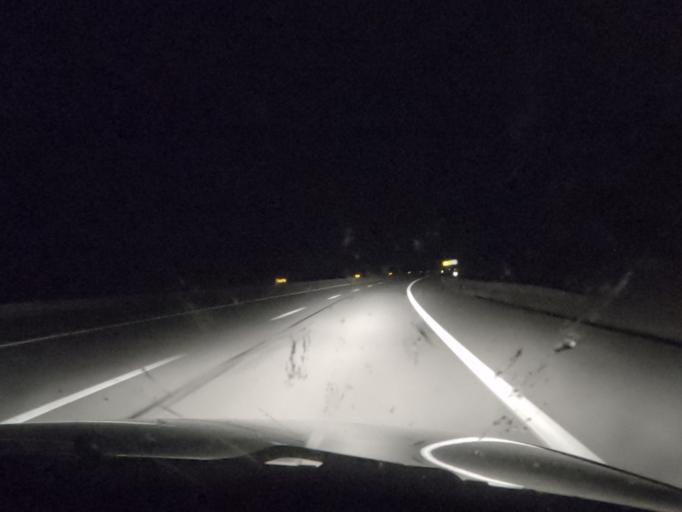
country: PT
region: Evora
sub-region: Estremoz
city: Estremoz
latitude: 38.8280
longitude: -7.6110
